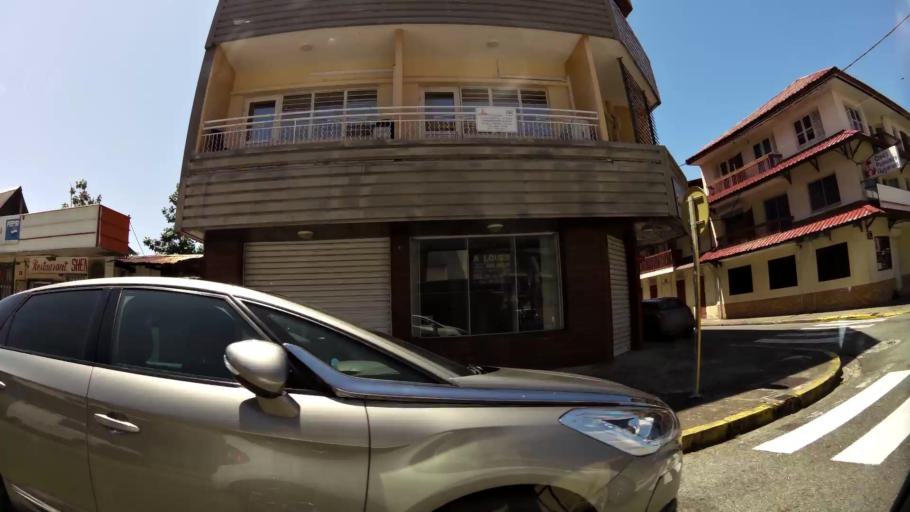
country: GF
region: Guyane
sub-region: Guyane
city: Cayenne
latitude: 4.9411
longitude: -52.3277
